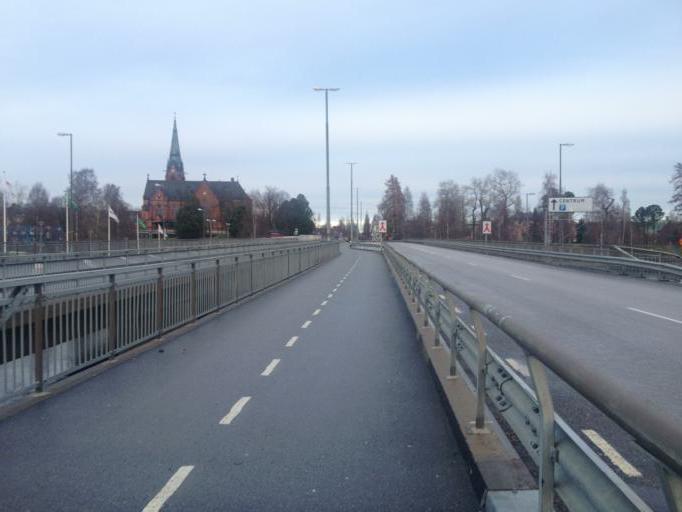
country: SE
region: Vaesterbotten
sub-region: Umea Kommun
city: Umea
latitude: 63.8213
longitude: 20.2674
